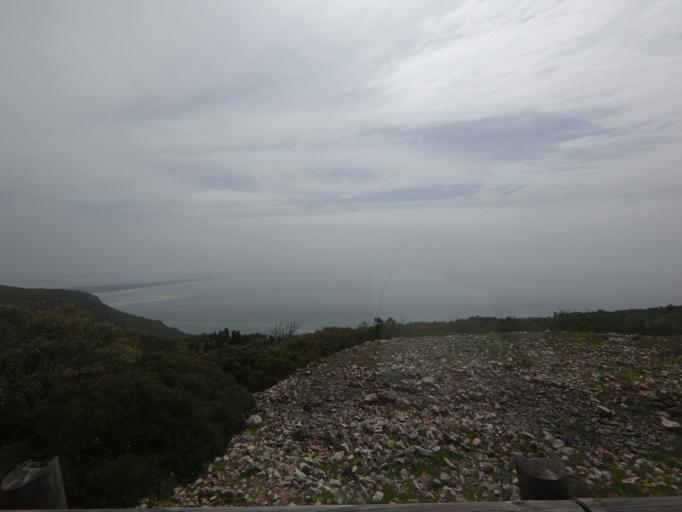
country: PT
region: Setubal
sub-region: Palmela
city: Quinta do Anjo
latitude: 38.4915
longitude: -8.9711
